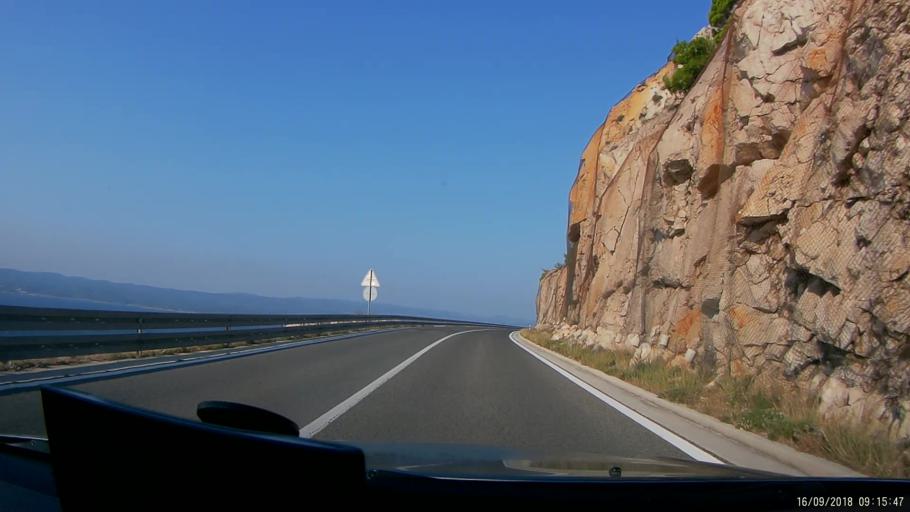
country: HR
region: Splitsko-Dalmatinska
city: Donja Brela
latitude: 43.3998
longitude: 16.8755
